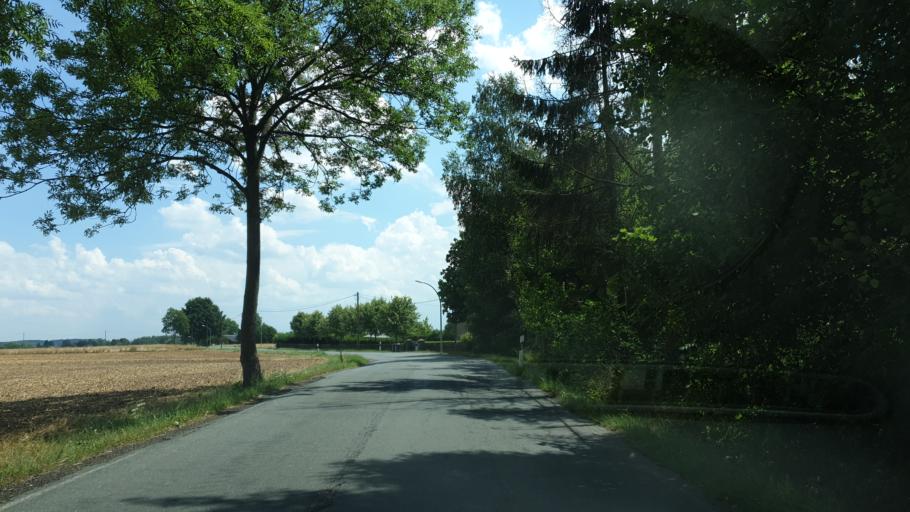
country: DE
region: Saxony
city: Kirchberg
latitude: 50.7991
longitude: 12.7782
